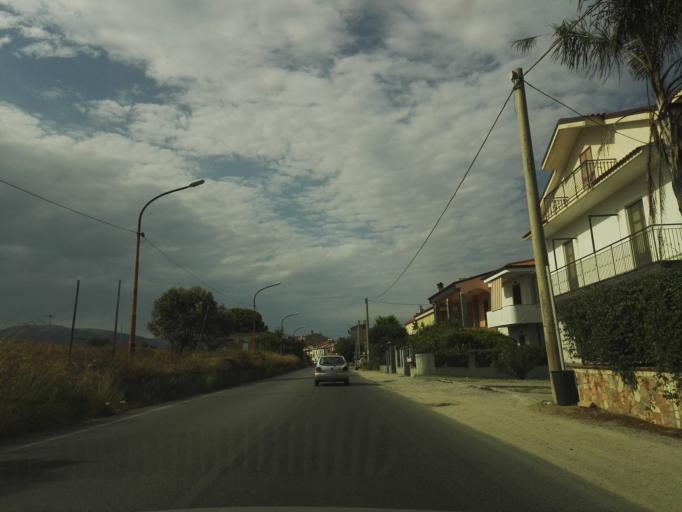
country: IT
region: Calabria
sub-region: Provincia di Catanzaro
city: Marina di Davoli
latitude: 38.6577
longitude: 16.5466
